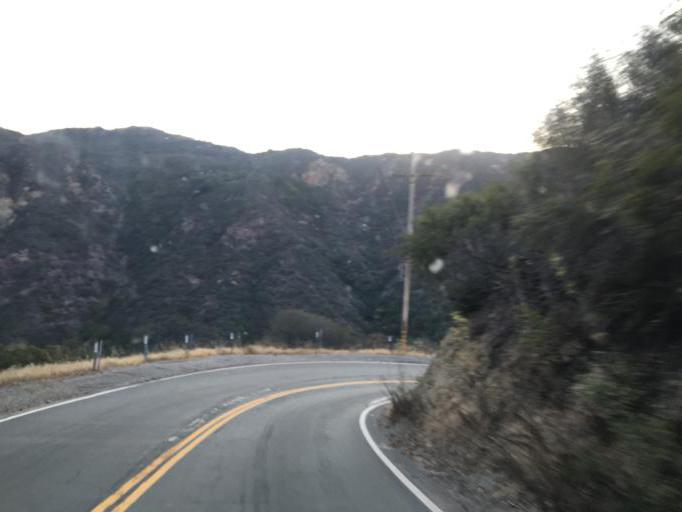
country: US
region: California
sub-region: Los Angeles County
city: Las Flores
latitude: 34.0669
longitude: -118.6412
